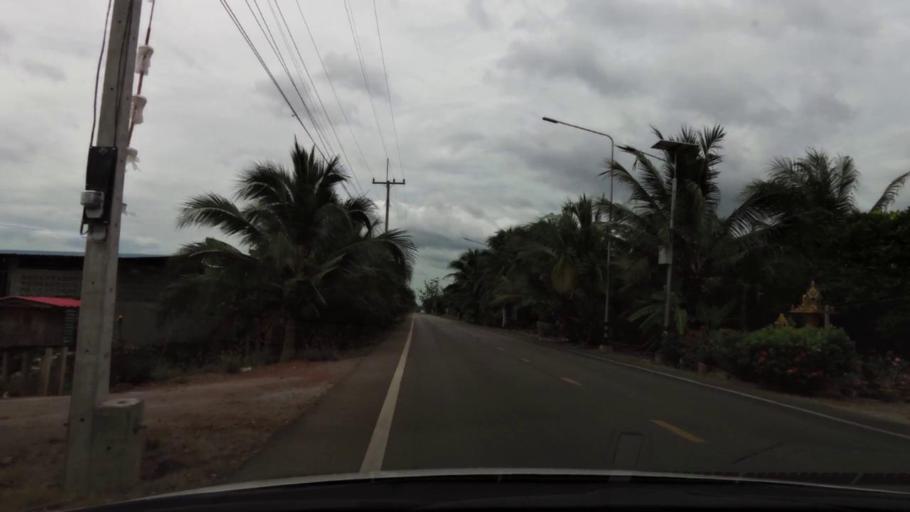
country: TH
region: Ratchaburi
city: Damnoen Saduak
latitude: 13.5635
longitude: 100.0127
